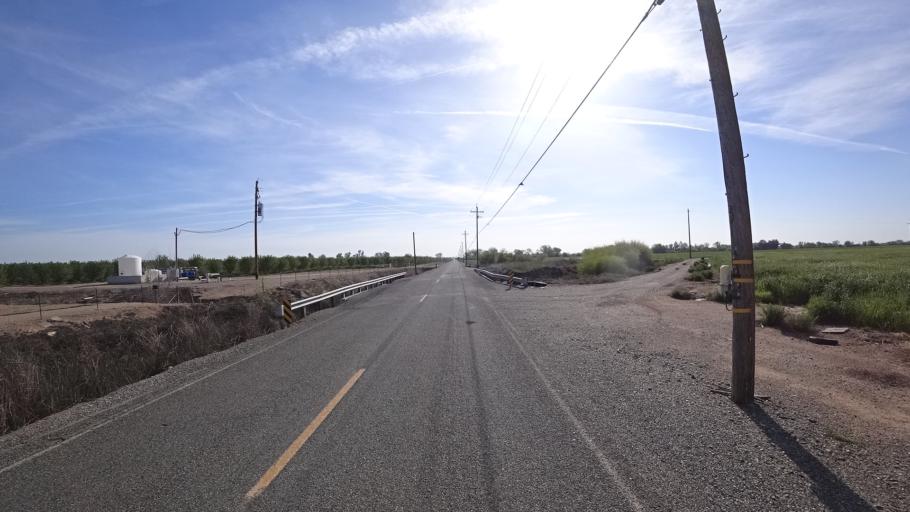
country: US
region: California
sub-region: Glenn County
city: Orland
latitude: 39.6681
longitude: -122.2264
